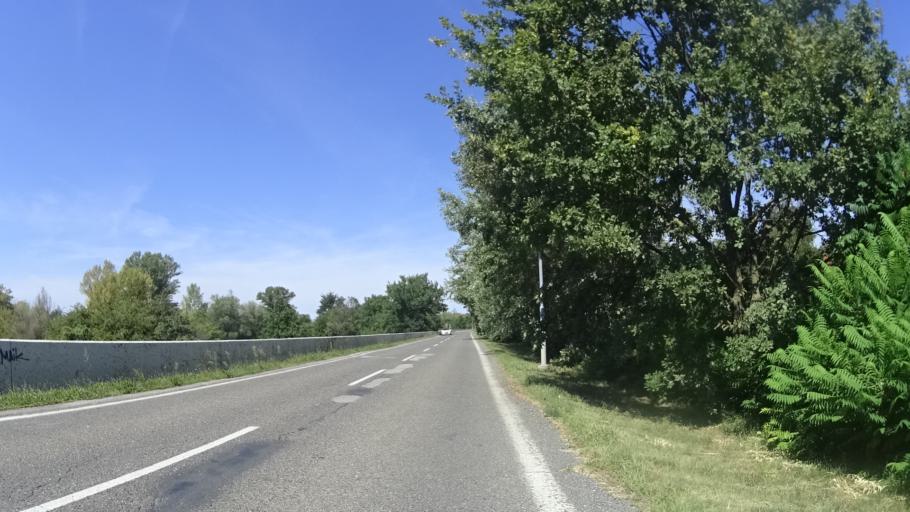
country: AT
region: Lower Austria
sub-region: Politischer Bezirk Bruck an der Leitha
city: Hainburg an der Donau
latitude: 48.2028
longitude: 16.9706
